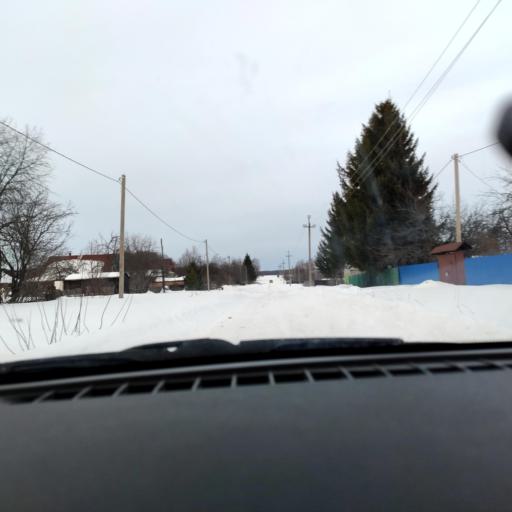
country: RU
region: Bashkortostan
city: Iglino
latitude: 54.7365
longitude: 56.5386
